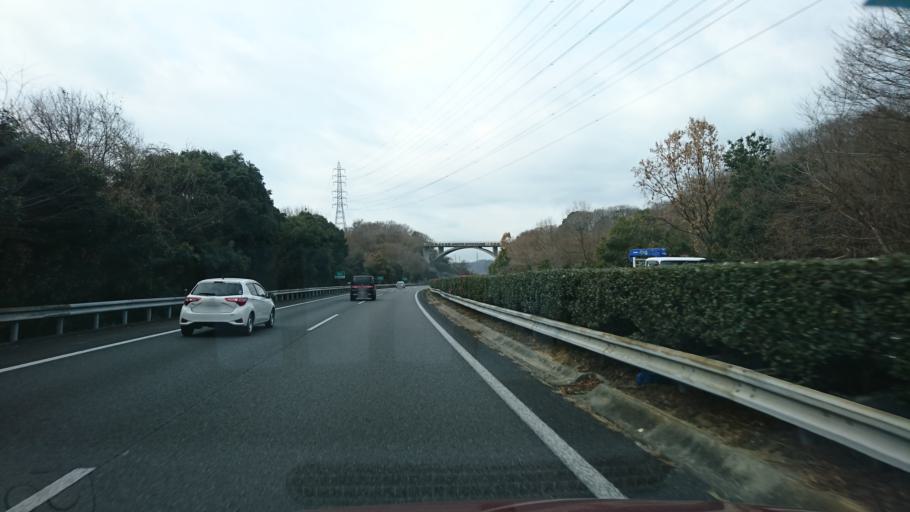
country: JP
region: Okayama
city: Kurashiki
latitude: 34.6045
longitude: 133.7229
